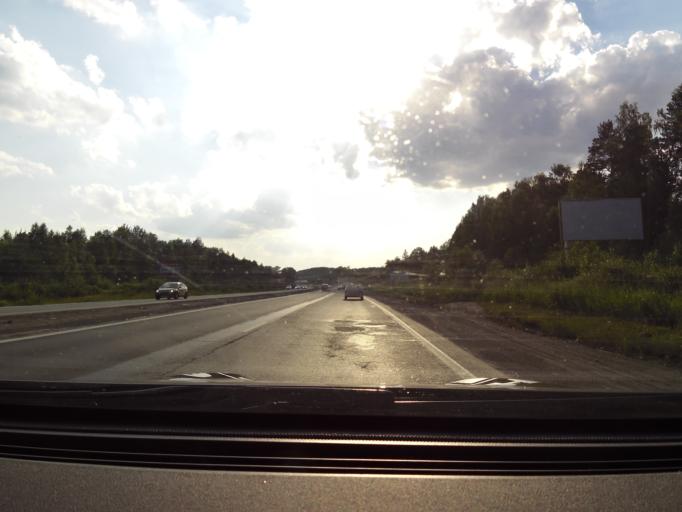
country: RU
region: Sverdlovsk
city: Severka
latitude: 56.8448
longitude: 60.2257
